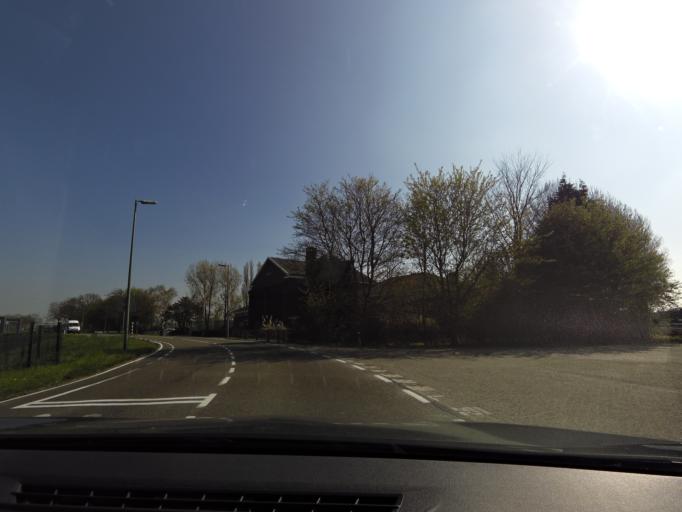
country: NL
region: South Holland
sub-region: Gemeente Maassluis
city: Maassluis
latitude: 51.9149
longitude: 4.2586
